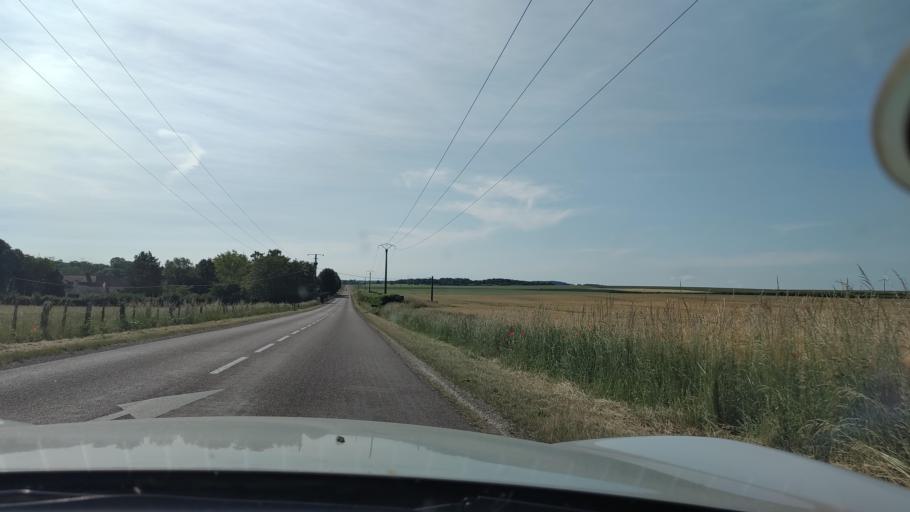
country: FR
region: Champagne-Ardenne
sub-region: Departement de l'Aube
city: Nogent-sur-Seine
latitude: 48.4872
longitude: 3.5297
